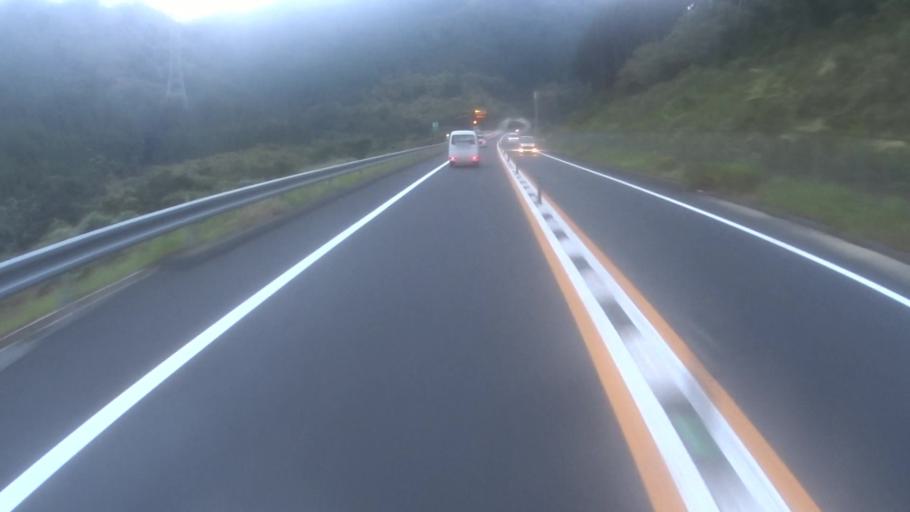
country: JP
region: Kyoto
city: Ayabe
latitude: 35.3132
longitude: 135.3220
